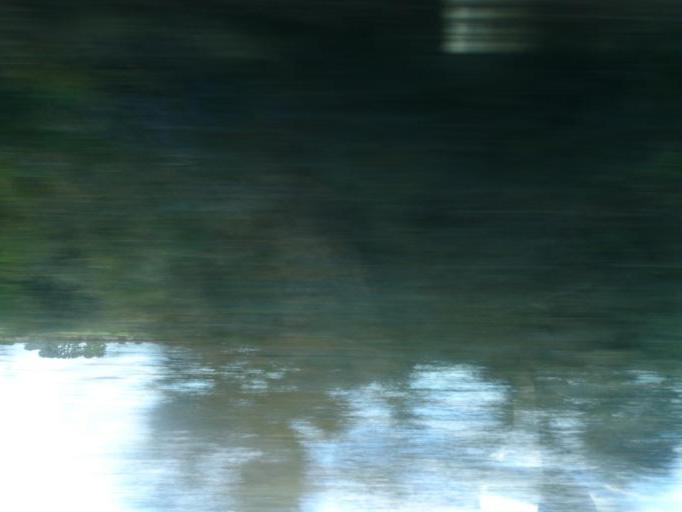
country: DE
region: Mecklenburg-Vorpommern
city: Anklam
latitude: 53.8739
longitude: 13.6897
